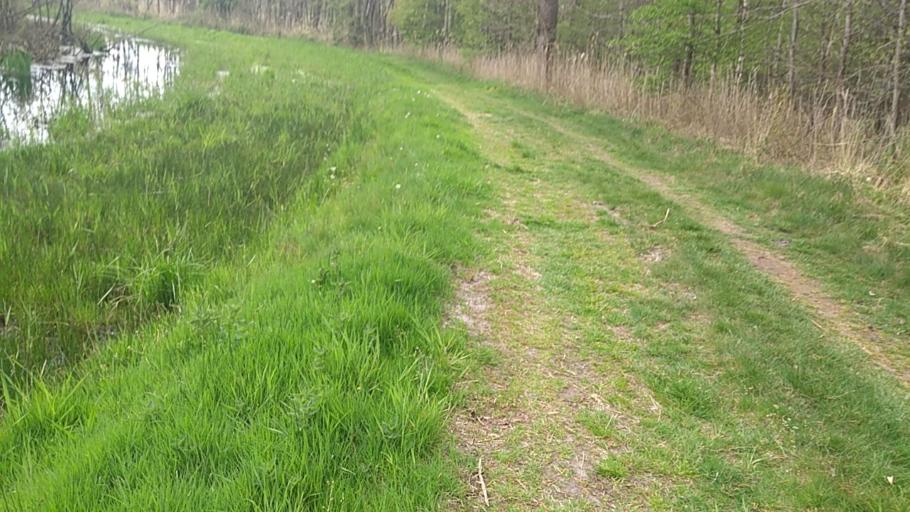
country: NL
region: Limburg
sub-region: Gemeente Leudal
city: Heythuysen
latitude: 51.2930
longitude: 5.8625
